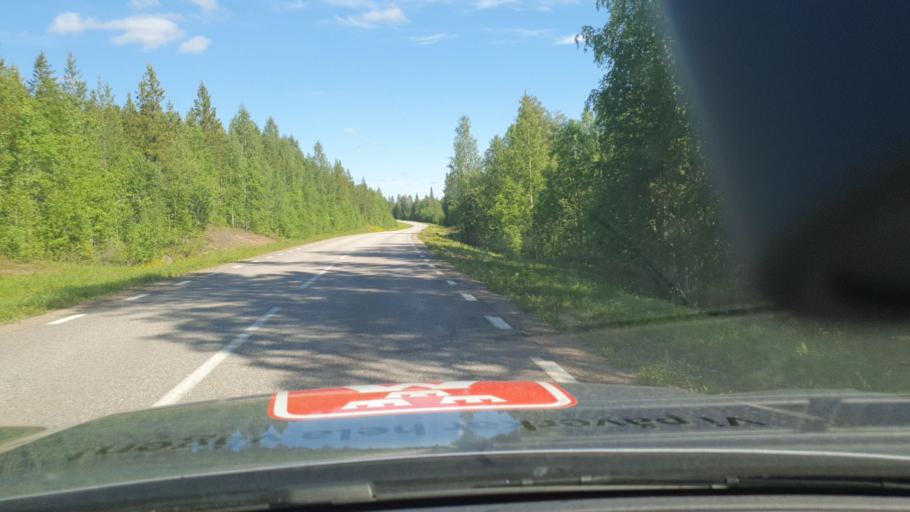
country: SE
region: Norrbotten
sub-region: Overkalix Kommun
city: OEverkalix
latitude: 66.6693
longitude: 22.6868
